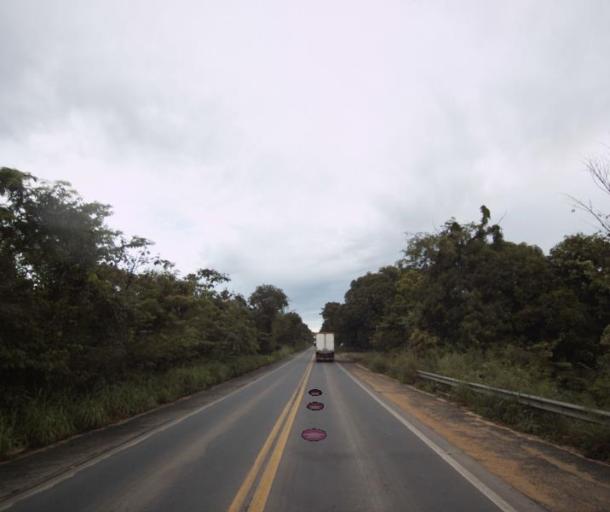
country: BR
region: Goias
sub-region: Porangatu
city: Porangatu
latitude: -13.7171
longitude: -49.0212
